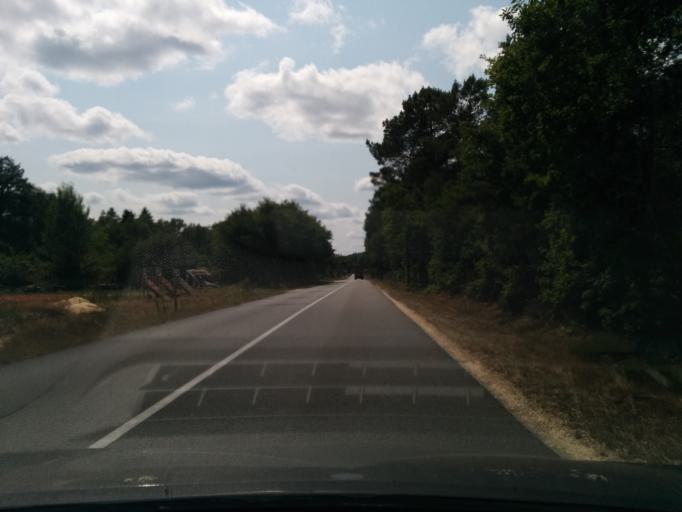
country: FR
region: Centre
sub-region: Departement du Cher
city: Neuvy-sur-Barangeon
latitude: 47.3198
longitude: 2.2694
